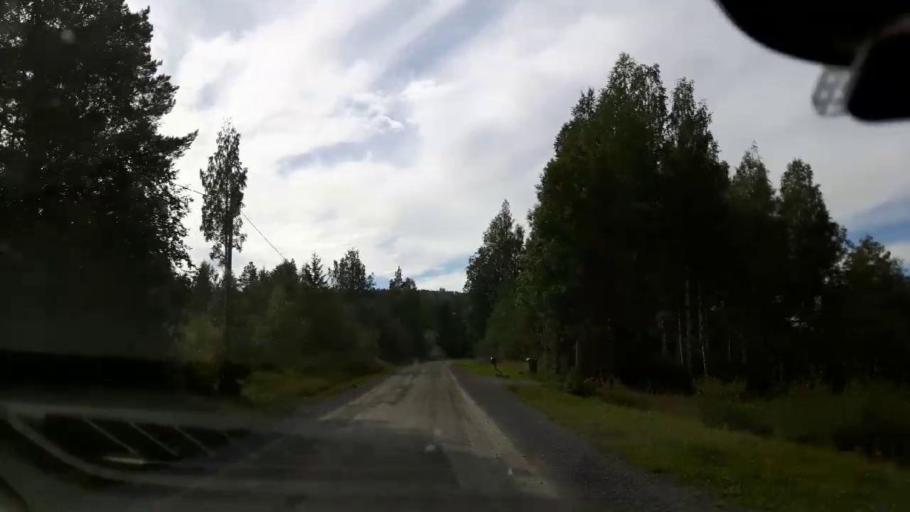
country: SE
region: Jaemtland
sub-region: Ragunda Kommun
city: Hammarstrand
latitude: 63.1359
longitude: 16.1460
